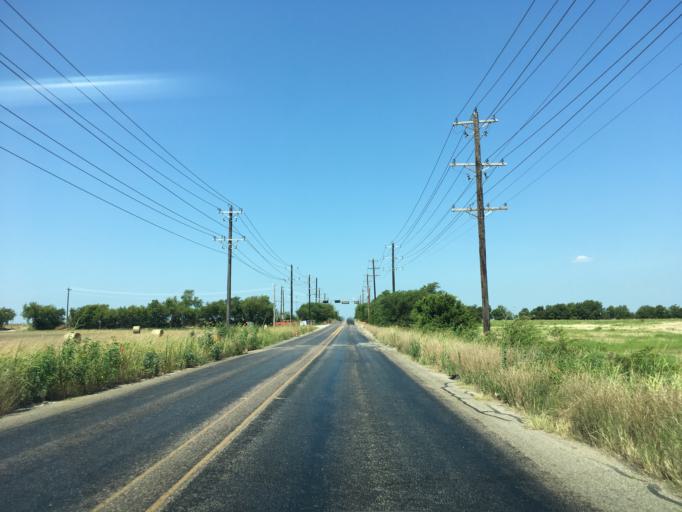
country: US
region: Texas
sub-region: Collin County
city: Prosper
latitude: 33.2039
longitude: -96.7835
